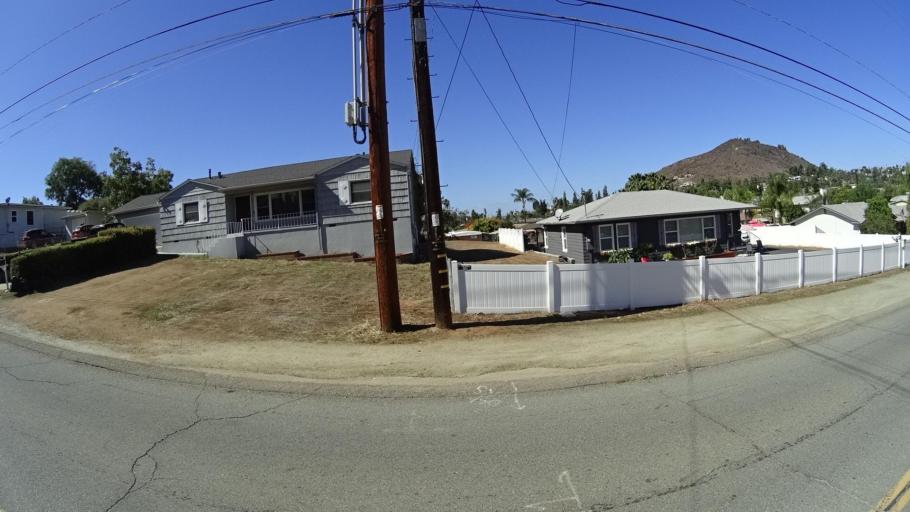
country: US
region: California
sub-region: San Diego County
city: Winter Gardens
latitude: 32.8199
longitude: -116.9303
